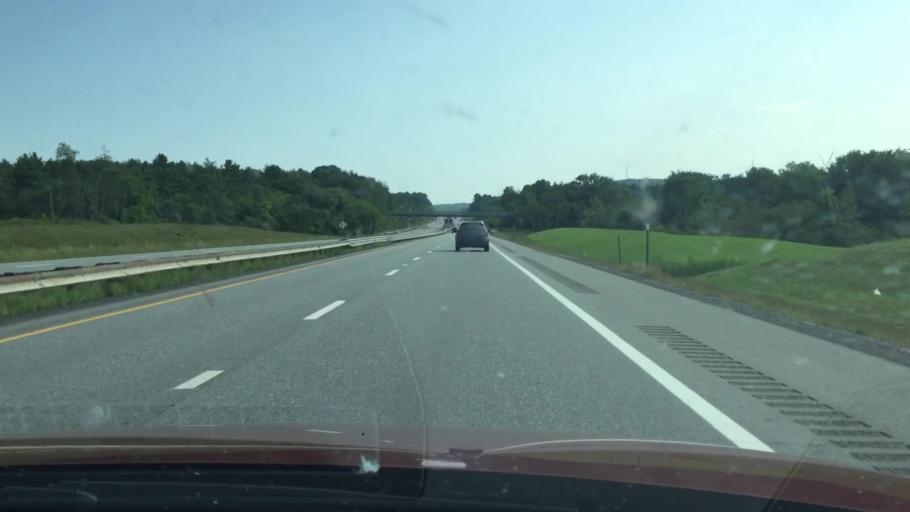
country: US
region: Maine
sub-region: Cumberland County
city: Cumberland Center
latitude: 43.7939
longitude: -70.3156
